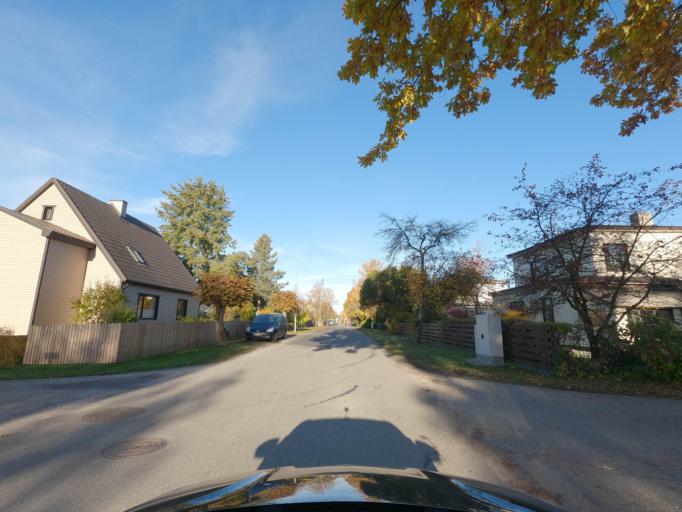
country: EE
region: Raplamaa
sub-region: Kohila vald
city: Kohila
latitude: 59.1658
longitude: 24.7621
